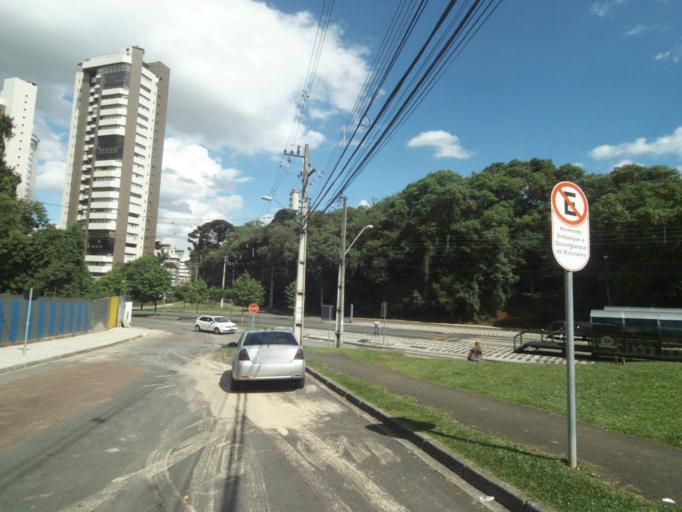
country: BR
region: Parana
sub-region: Curitiba
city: Curitiba
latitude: -25.4384
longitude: -49.3332
